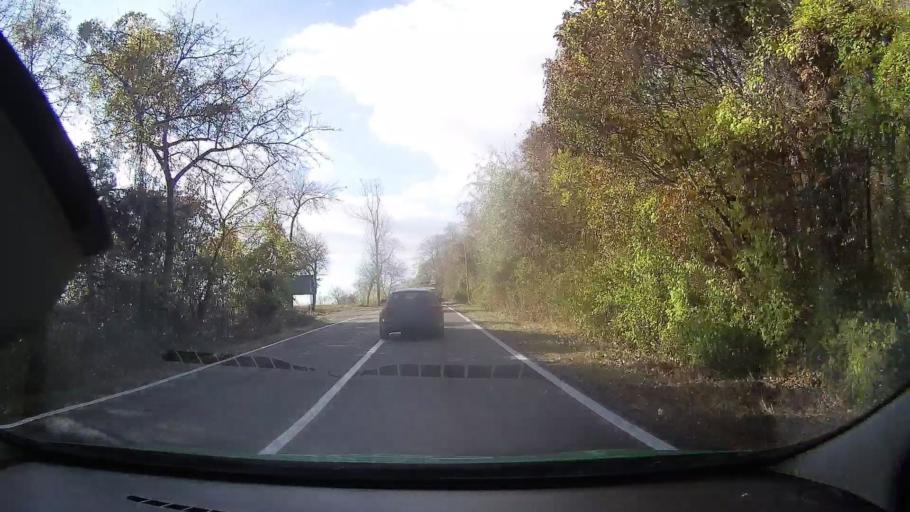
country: RO
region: Tulcea
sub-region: Comuna Topolog
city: Topolog
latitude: 44.9073
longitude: 28.4096
